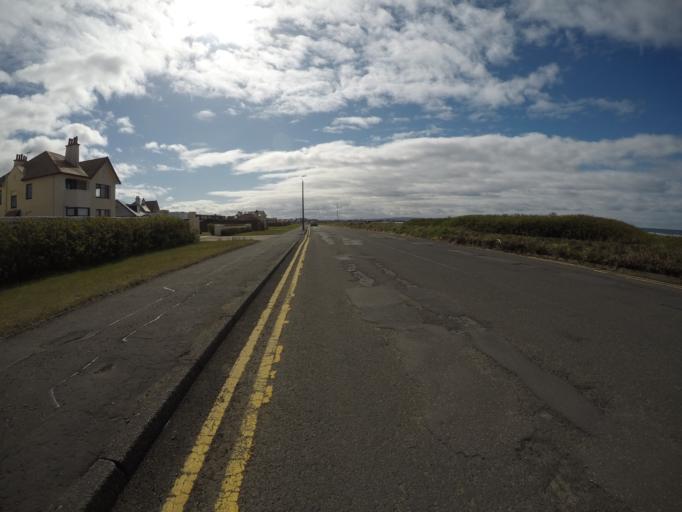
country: GB
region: Scotland
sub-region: South Ayrshire
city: Troon
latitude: 55.5649
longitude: -4.6581
